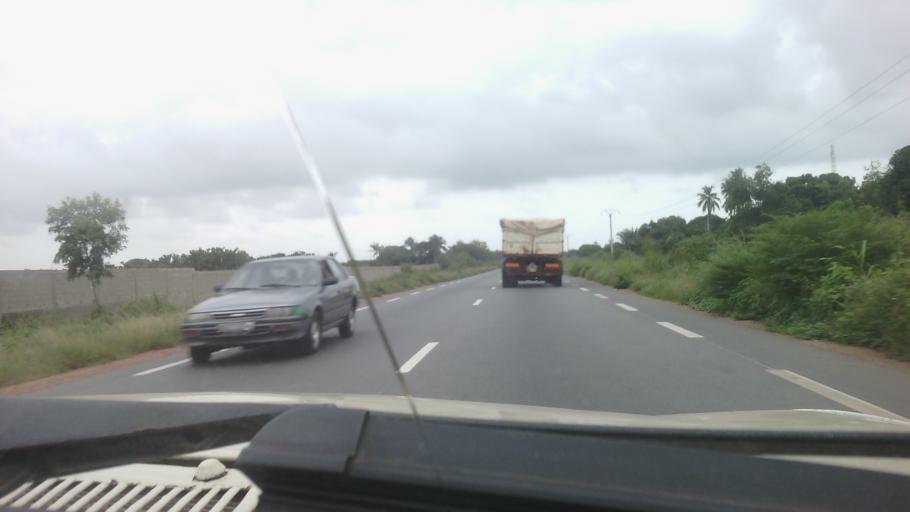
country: BJ
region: Atlantique
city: Ouidah
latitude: 6.3764
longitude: 2.0276
